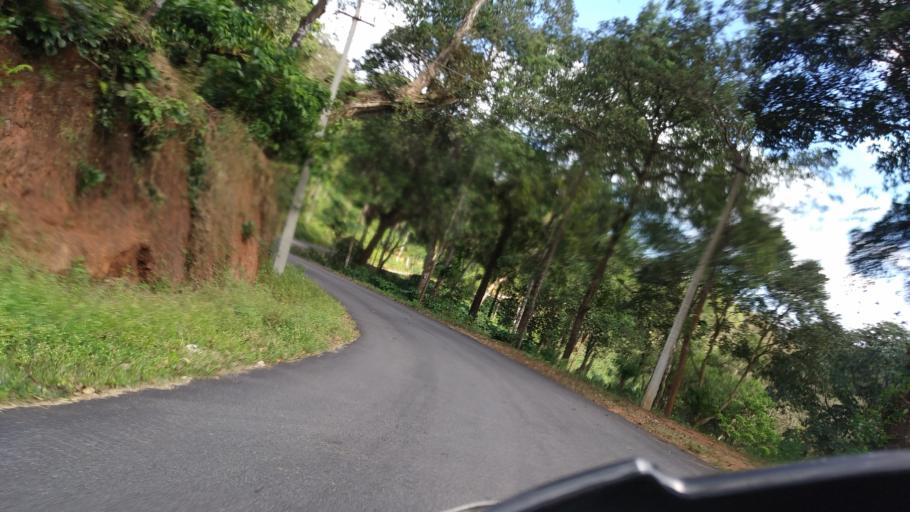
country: IN
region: Karnataka
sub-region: Kodagu
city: Ponnampet
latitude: 12.0313
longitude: 75.9218
